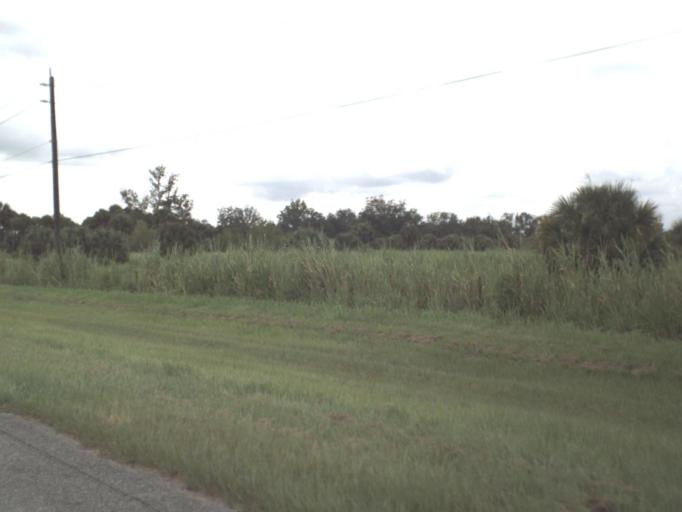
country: US
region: Florida
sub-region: Lee County
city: Alva
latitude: 26.7095
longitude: -81.5690
